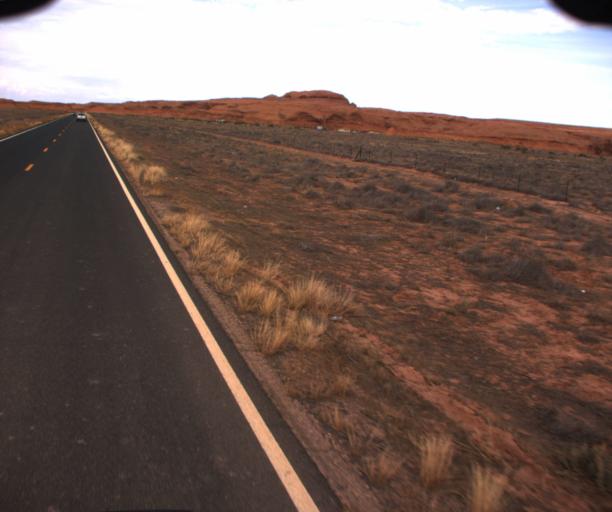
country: US
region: Arizona
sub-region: Apache County
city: Many Farms
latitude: 36.7535
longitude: -109.6452
